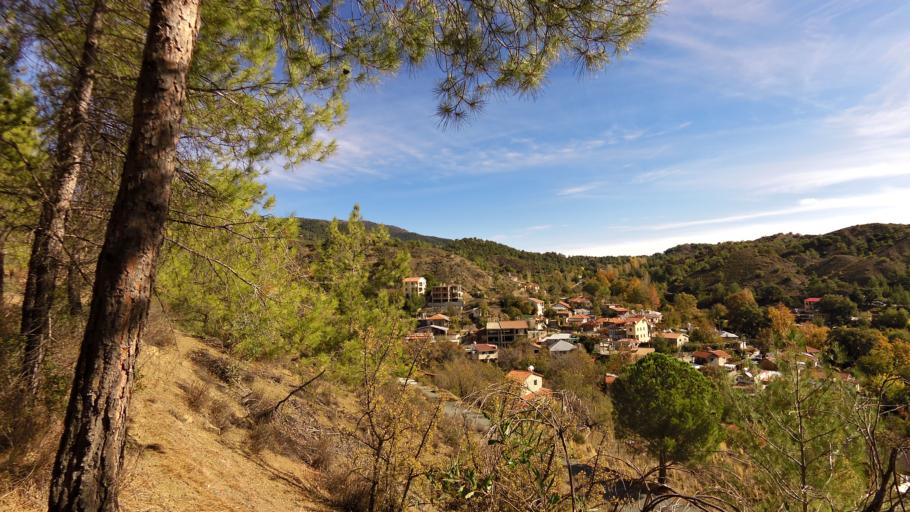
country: CY
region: Limassol
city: Pachna
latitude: 34.8802
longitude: 32.8393
